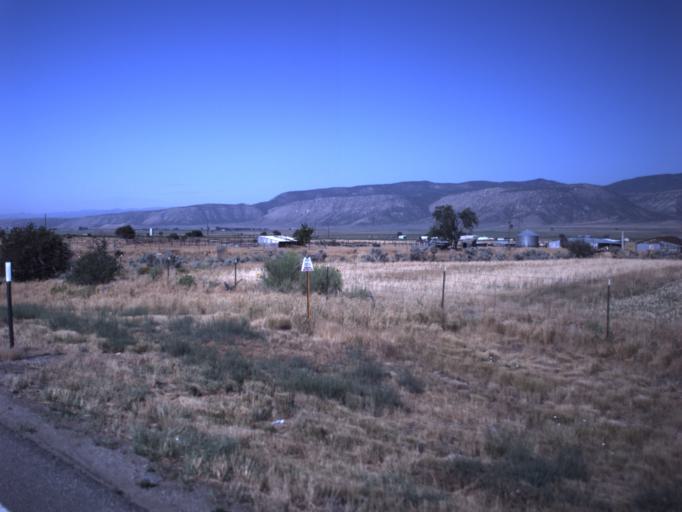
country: US
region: Utah
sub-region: Sanpete County
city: Ephraim
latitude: 39.3320
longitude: -111.5993
